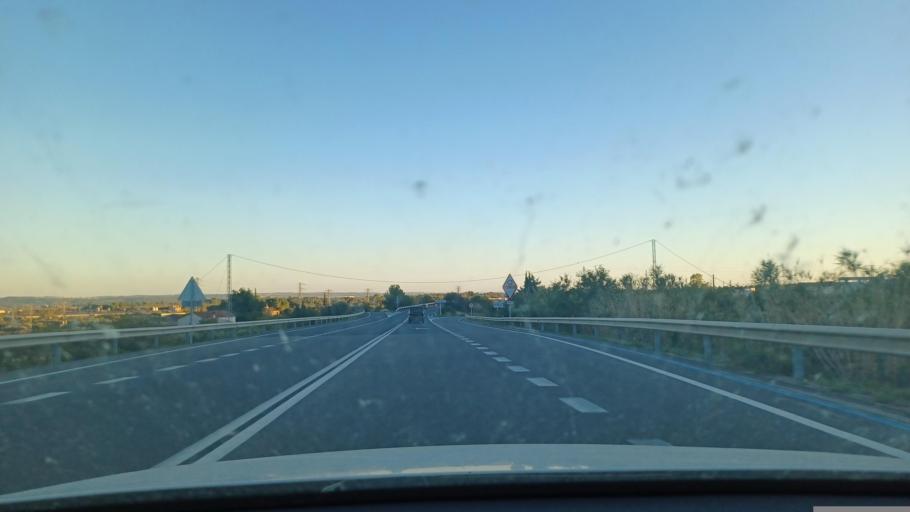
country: ES
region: Catalonia
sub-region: Provincia de Tarragona
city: Alcover
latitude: 41.2659
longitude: 1.1757
